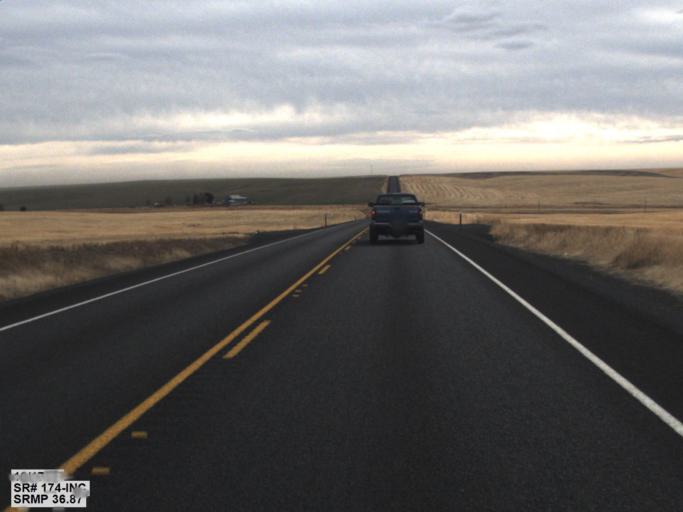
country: US
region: Washington
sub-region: Okanogan County
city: Coulee Dam
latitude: 47.8143
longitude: -118.7726
